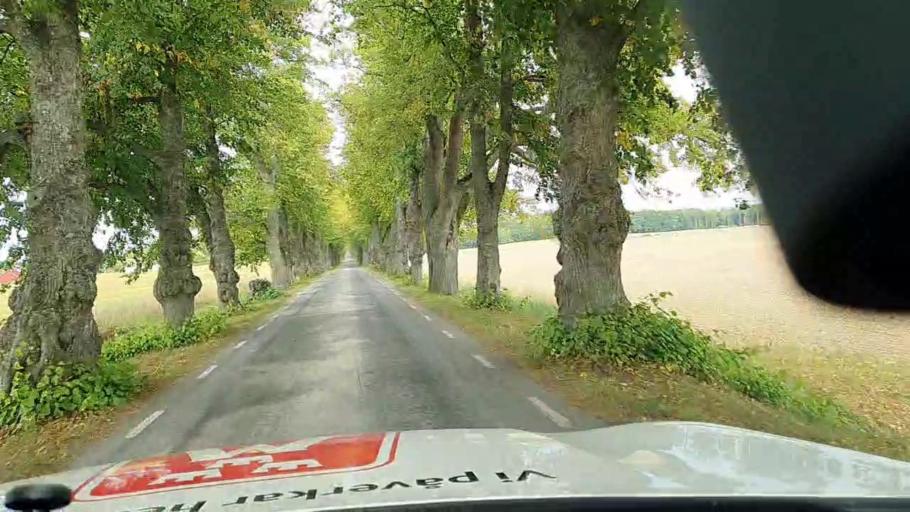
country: SE
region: Soedermanland
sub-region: Nykopings Kommun
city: Svalsta
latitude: 58.8183
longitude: 16.8957
